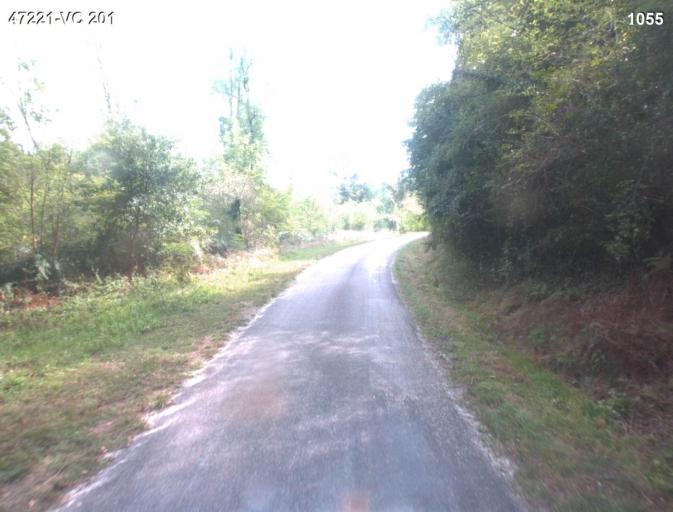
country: FR
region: Aquitaine
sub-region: Departement du Lot-et-Garonne
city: Mezin
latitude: 44.1137
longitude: 0.2329
